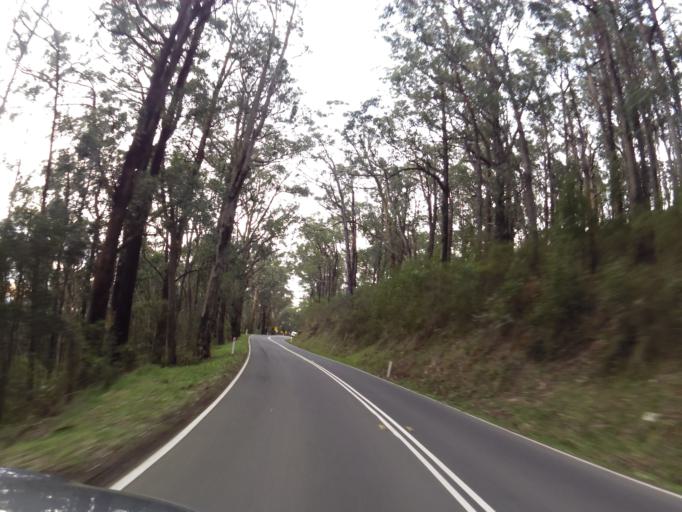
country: AU
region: Victoria
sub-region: Yarra Ranges
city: Ferny Creek
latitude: -37.8629
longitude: 145.3380
